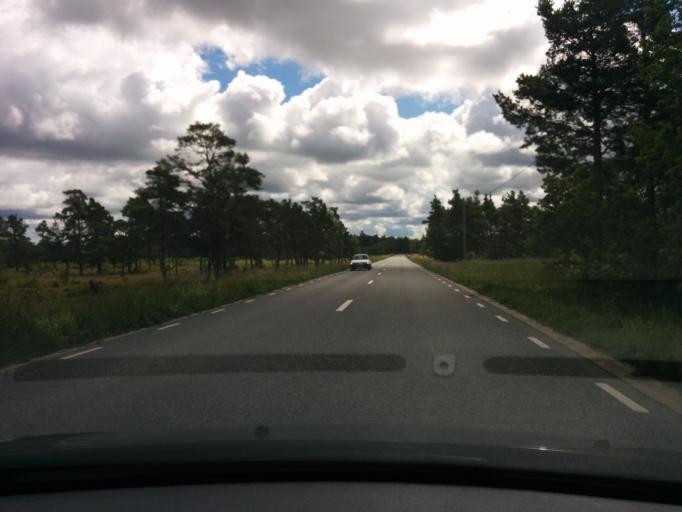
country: SE
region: Gotland
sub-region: Gotland
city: Visby
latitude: 57.6374
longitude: 18.5238
